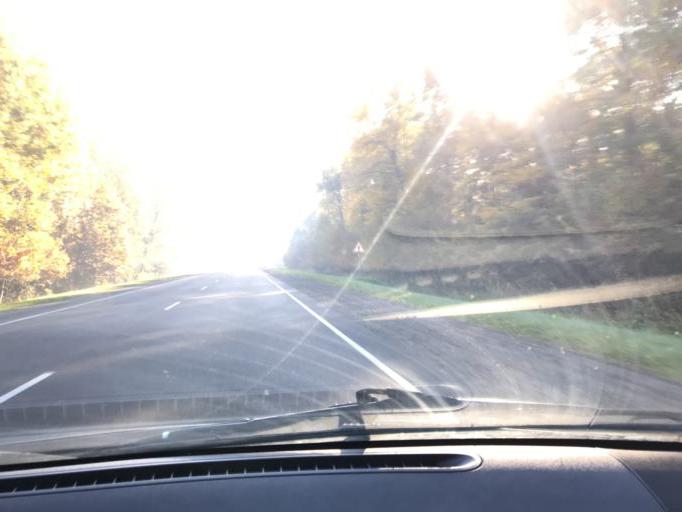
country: BY
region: Brest
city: Horad Luninyets
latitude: 52.3087
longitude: 26.6801
